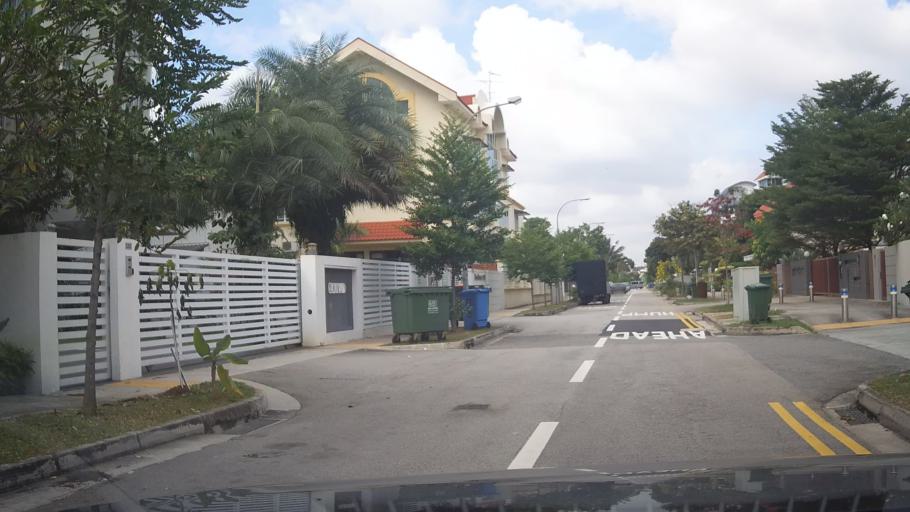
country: SG
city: Singapore
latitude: 1.3125
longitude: 103.9143
